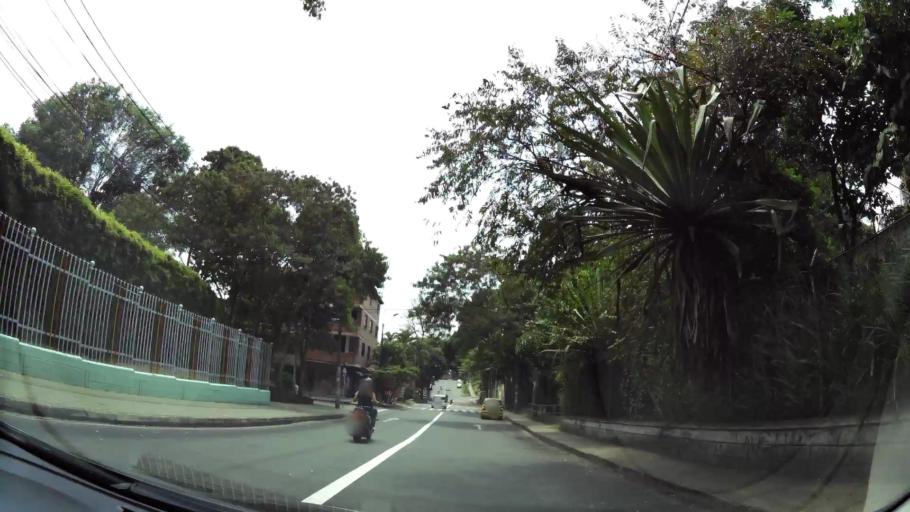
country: CO
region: Antioquia
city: Bello
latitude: 6.3000
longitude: -75.5679
